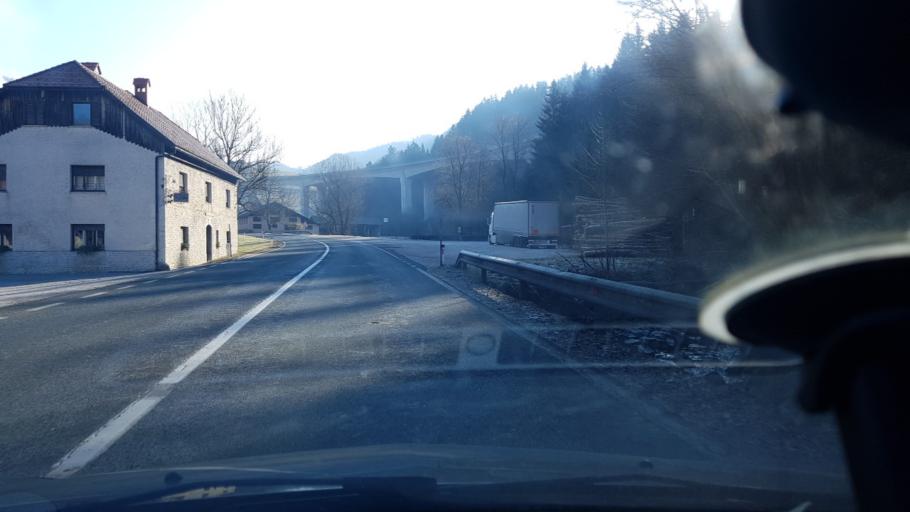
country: SI
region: Moravce
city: Moravce
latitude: 46.1775
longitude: 14.8189
